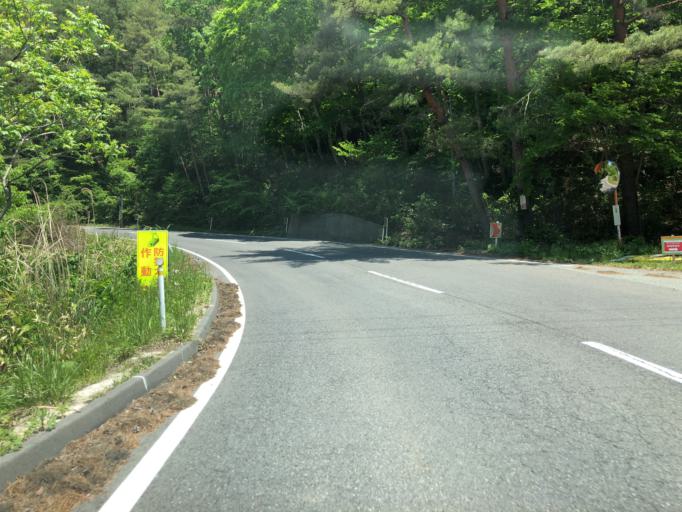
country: JP
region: Fukushima
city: Funehikimachi-funehiki
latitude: 37.5040
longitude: 140.7748
